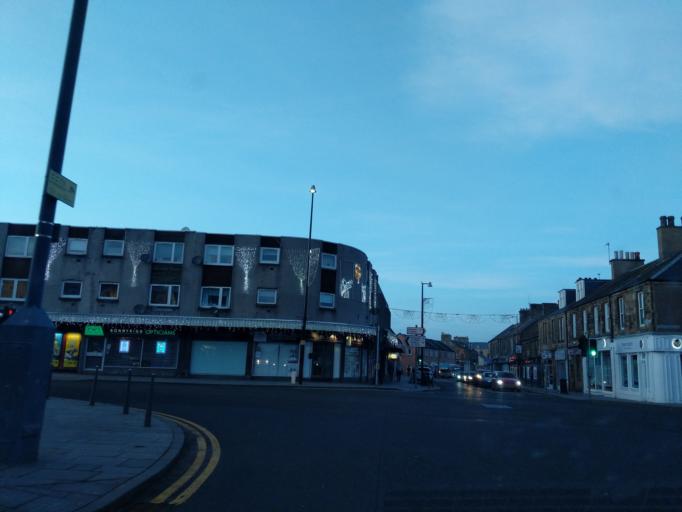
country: GB
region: Scotland
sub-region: Midlothian
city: Bonnyrigg
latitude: 55.8747
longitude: -3.1055
